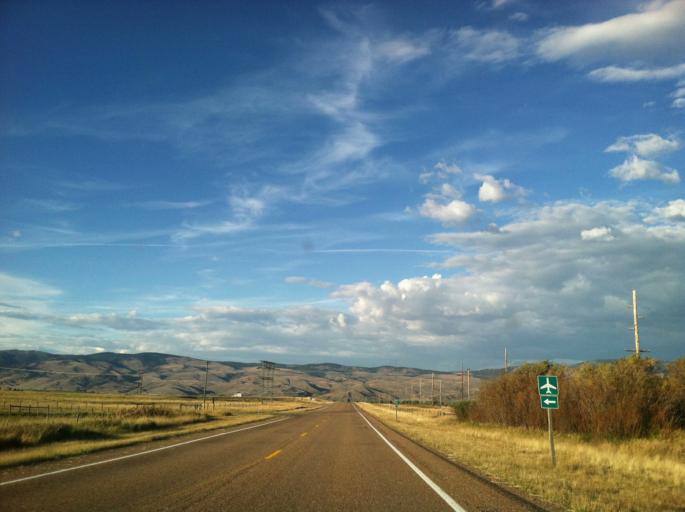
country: US
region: Montana
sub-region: Granite County
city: Philipsburg
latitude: 46.6173
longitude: -113.1752
